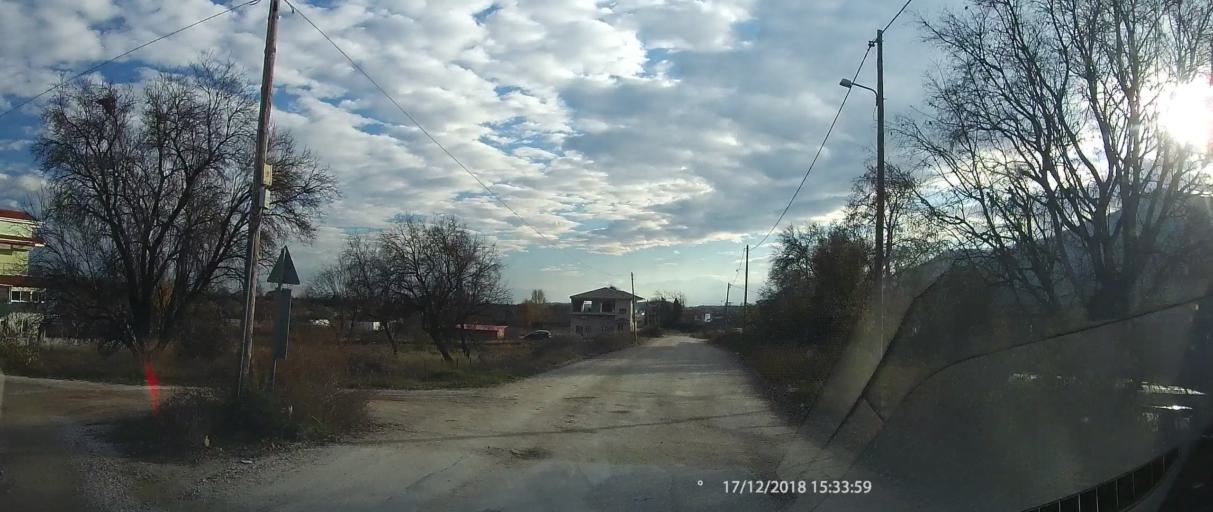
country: GR
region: Thessaly
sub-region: Trikala
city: Kalampaka
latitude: 39.7001
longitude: 21.6330
